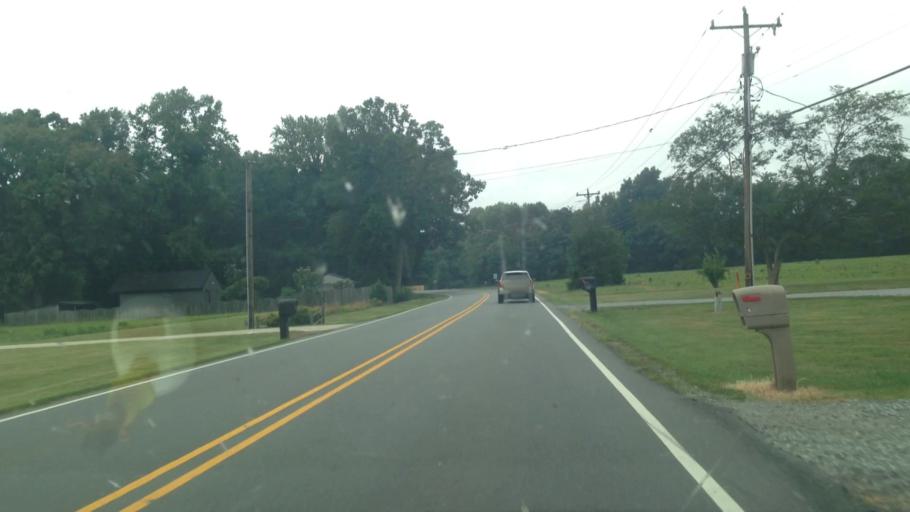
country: US
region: North Carolina
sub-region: Forsyth County
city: Walkertown
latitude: 36.1465
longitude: -80.1278
